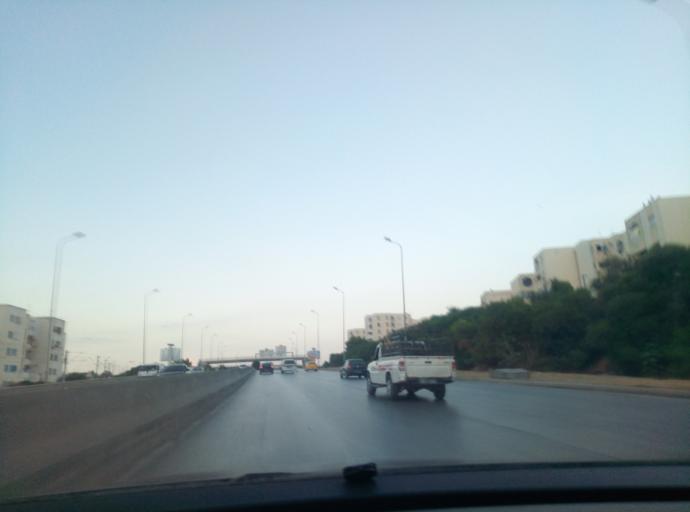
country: TN
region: Tunis
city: Tunis
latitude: 36.8236
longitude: 10.1419
